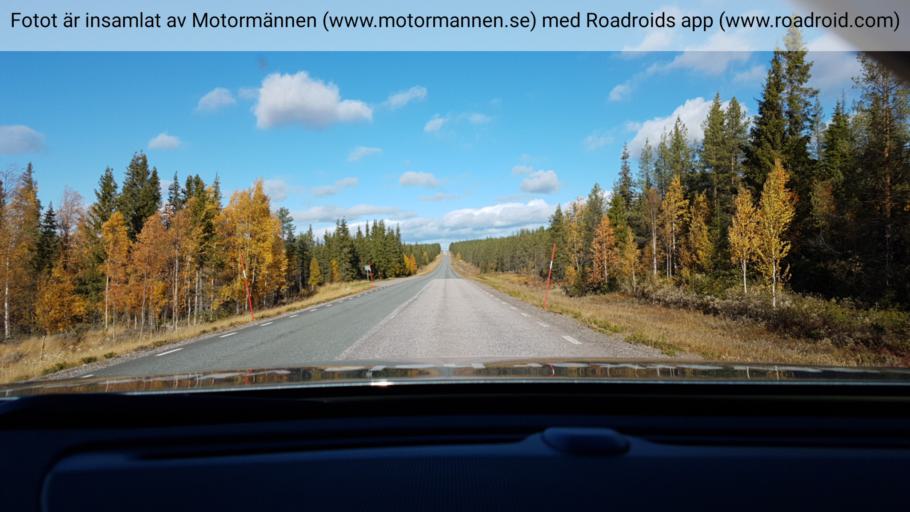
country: SE
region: Norrbotten
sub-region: Arjeplogs Kommun
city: Arjeplog
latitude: 65.8202
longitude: 18.4408
